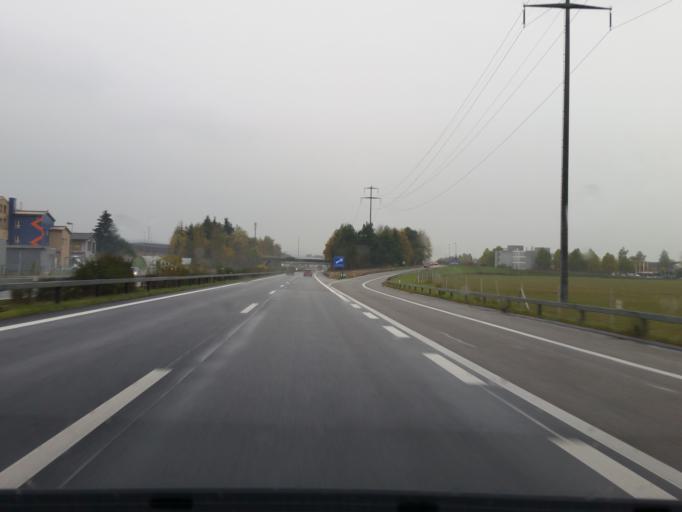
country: CH
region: Thurgau
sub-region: Frauenfeld District
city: Frauenfeld
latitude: 47.5713
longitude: 8.9101
